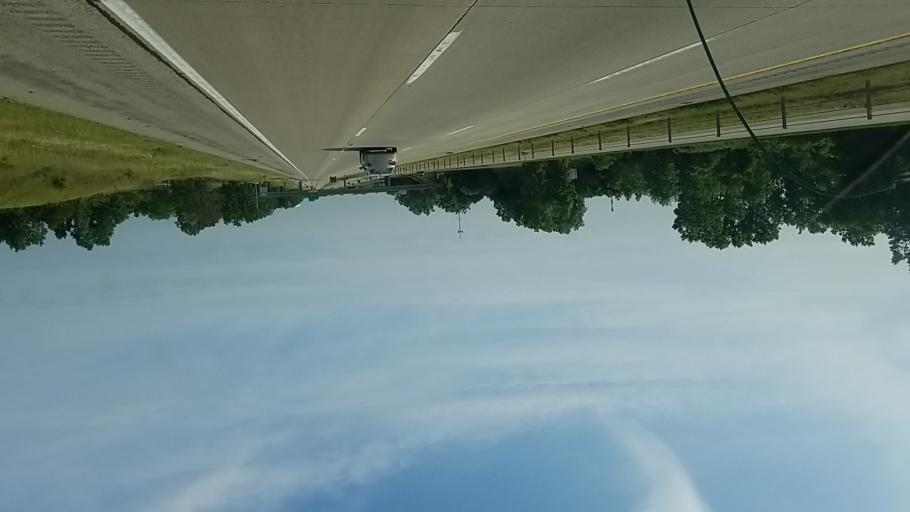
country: US
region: Michigan
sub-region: Eaton County
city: Waverly
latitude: 42.7155
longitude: -84.6693
